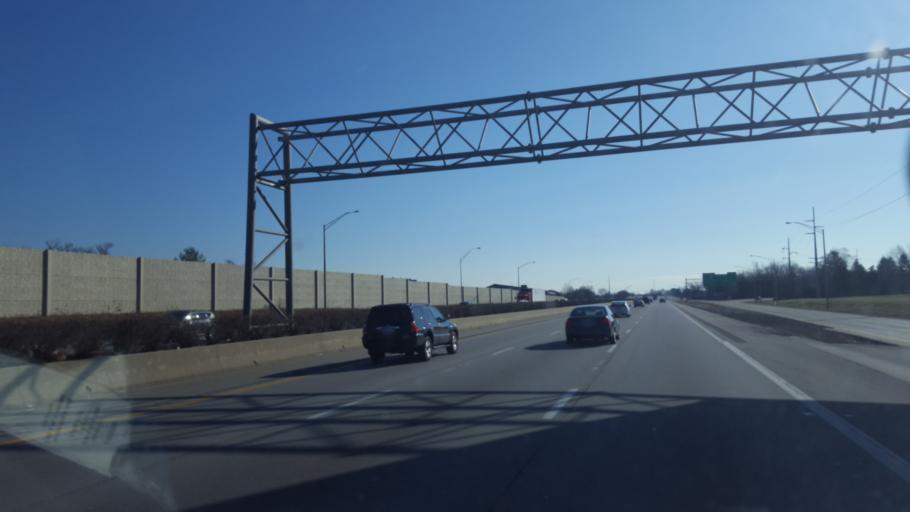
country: US
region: Kentucky
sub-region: Jefferson County
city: Hurstbourne Acres
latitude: 38.2266
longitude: -85.5892
